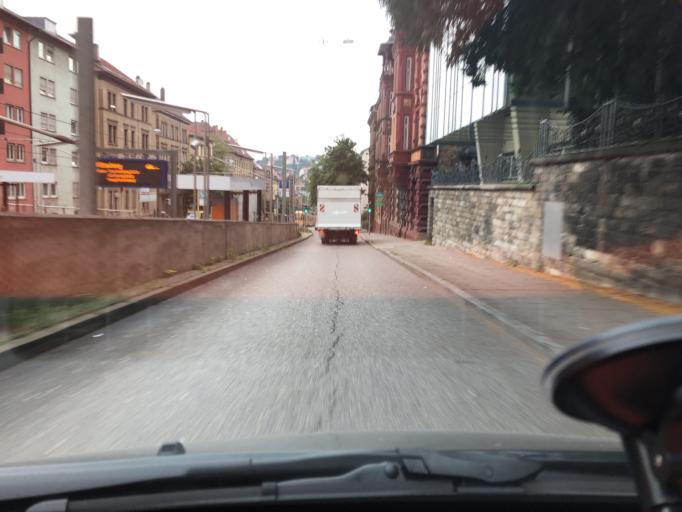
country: DE
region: Baden-Wuerttemberg
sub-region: Regierungsbezirk Stuttgart
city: Stuttgart
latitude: 48.7678
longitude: 9.1837
